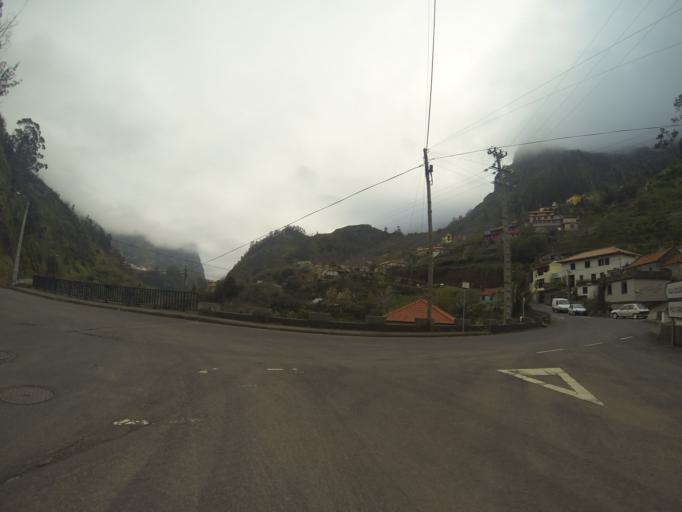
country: PT
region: Madeira
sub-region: Camara de Lobos
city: Curral das Freiras
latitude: 32.7300
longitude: -16.9674
